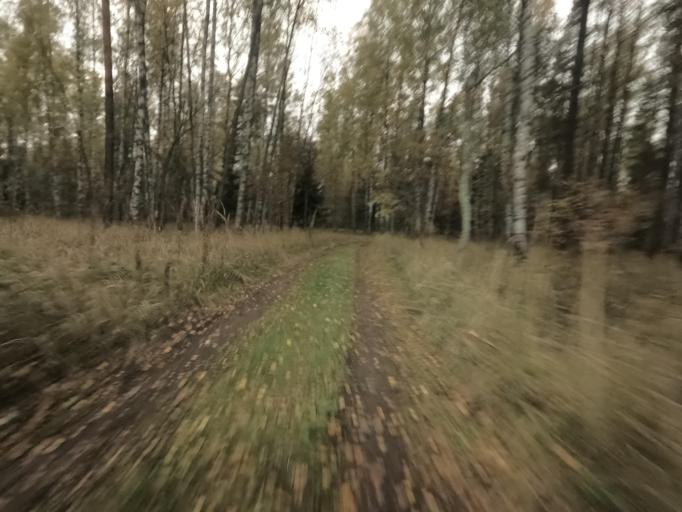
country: RU
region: Leningrad
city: Kirovsk
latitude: 59.8317
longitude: 30.9780
